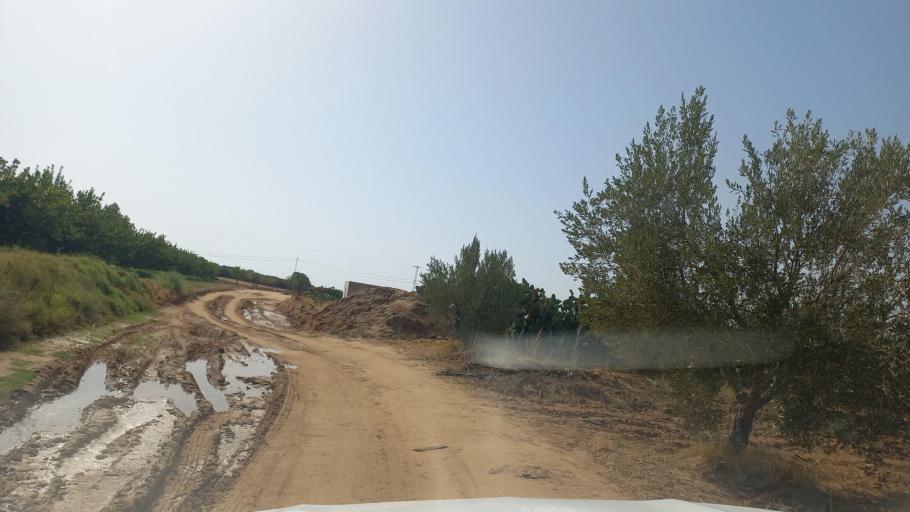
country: TN
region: Al Qasrayn
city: Kasserine
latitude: 35.2417
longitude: 9.0362
